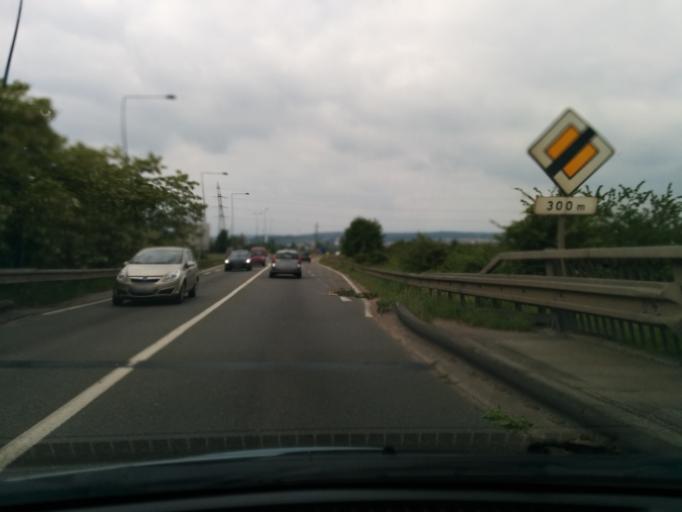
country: FR
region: Ile-de-France
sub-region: Departement des Yvelines
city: Epone
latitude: 48.9636
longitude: 1.8115
